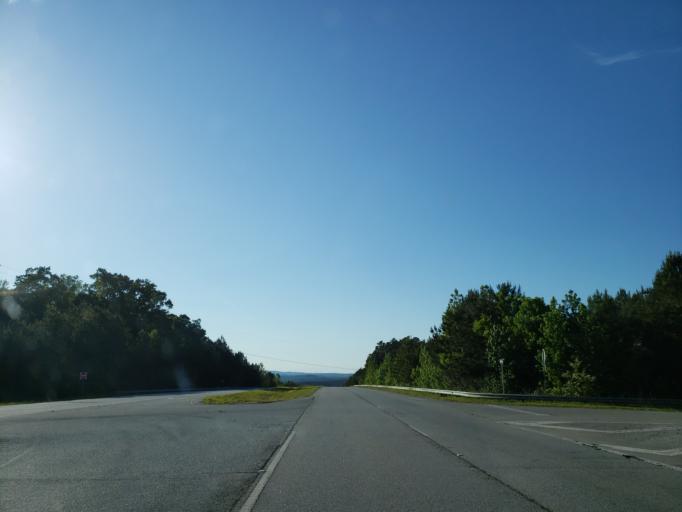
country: US
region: Georgia
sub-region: Haralson County
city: Buchanan
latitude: 33.9087
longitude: -85.2393
